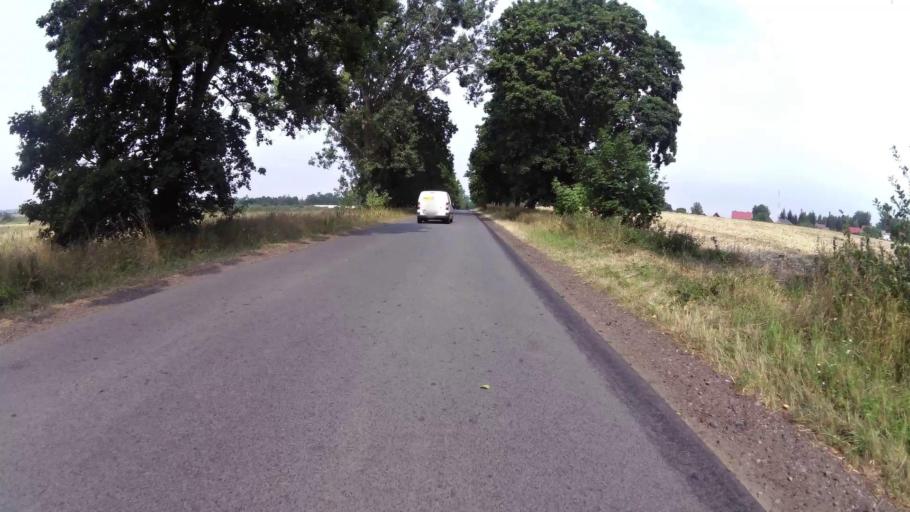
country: PL
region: West Pomeranian Voivodeship
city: Trzcinsko Zdroj
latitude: 52.9590
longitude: 14.6205
